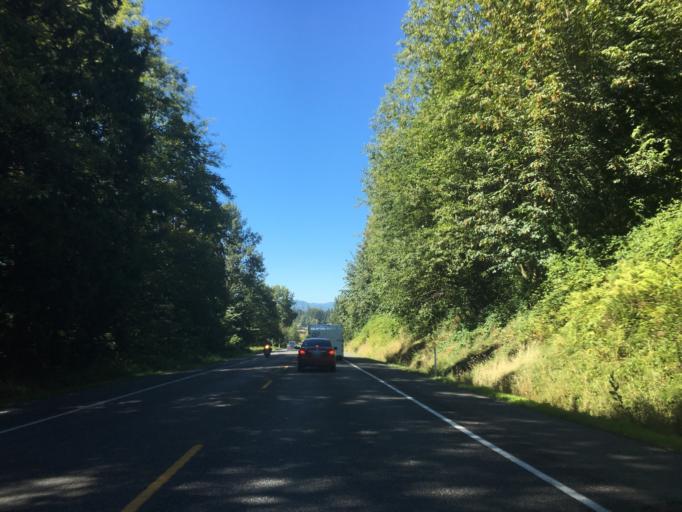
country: US
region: Washington
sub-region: Snohomish County
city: Arlington
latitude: 48.1743
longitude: -122.1256
